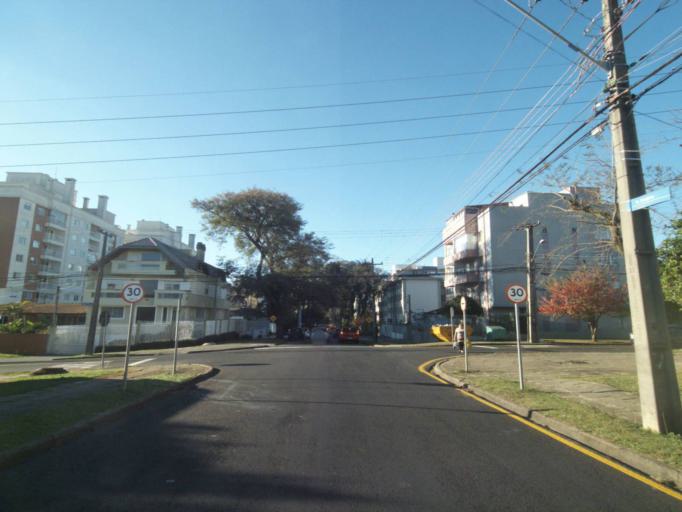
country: BR
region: Parana
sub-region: Curitiba
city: Curitiba
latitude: -25.4586
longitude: -49.2975
